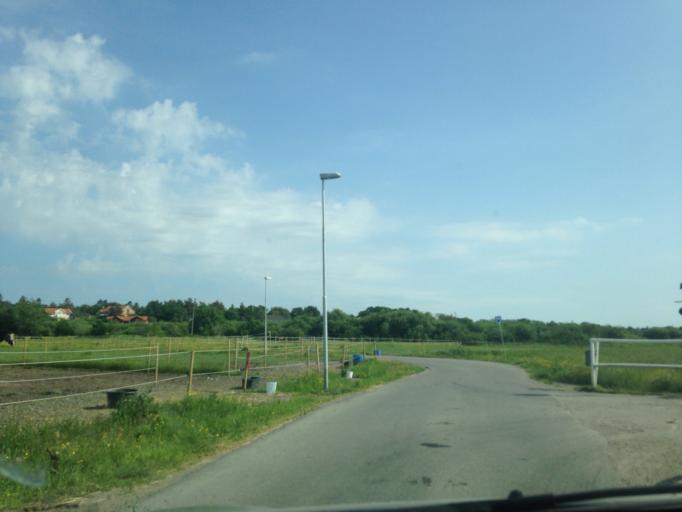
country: SE
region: Vaestra Goetaland
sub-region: Goteborg
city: Torslanda
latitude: 57.7749
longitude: 11.8317
